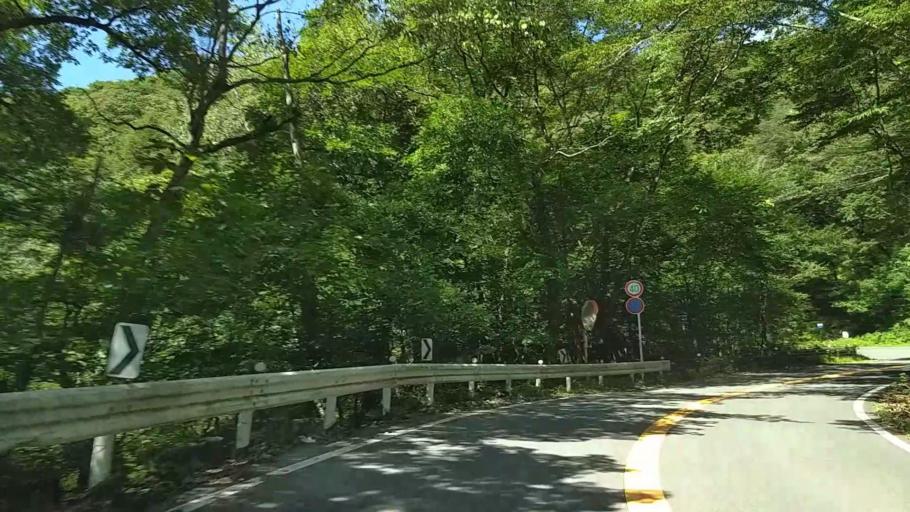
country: JP
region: Nagano
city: Saku
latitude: 36.3462
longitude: 138.6520
